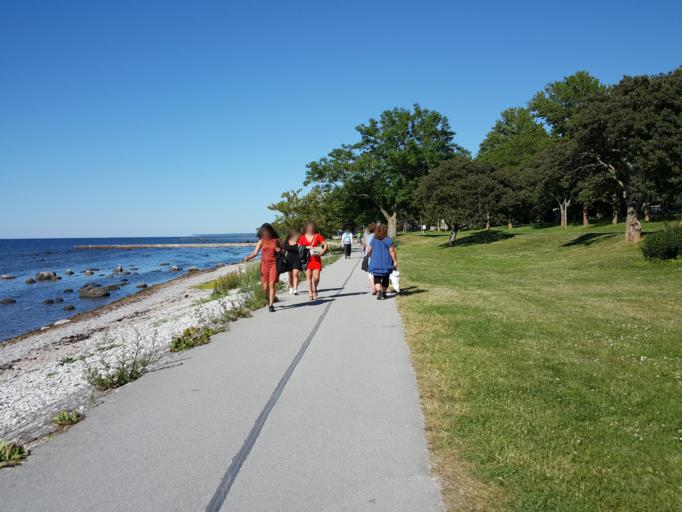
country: SE
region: Gotland
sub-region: Gotland
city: Visby
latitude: 57.6475
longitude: 18.2965
